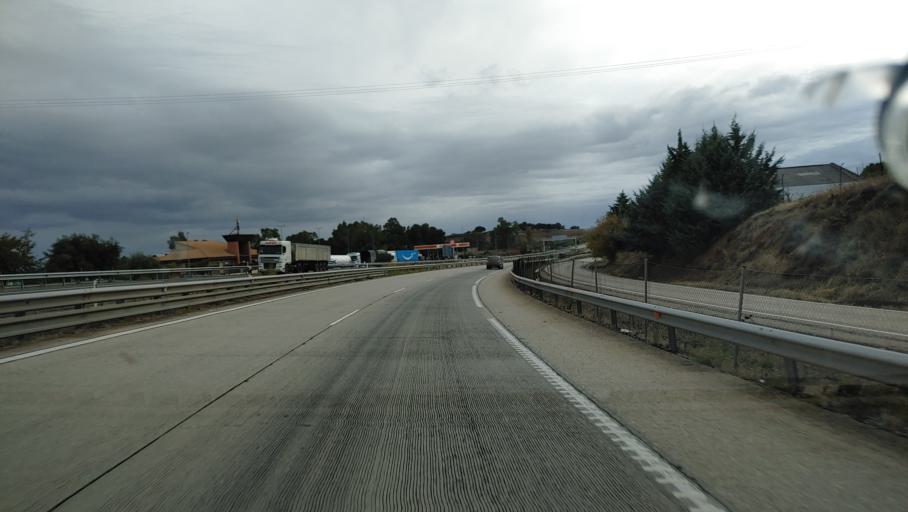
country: ES
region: Andalusia
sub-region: Provincia de Jaen
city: Santa Elena
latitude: 38.3314
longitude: -3.5436
